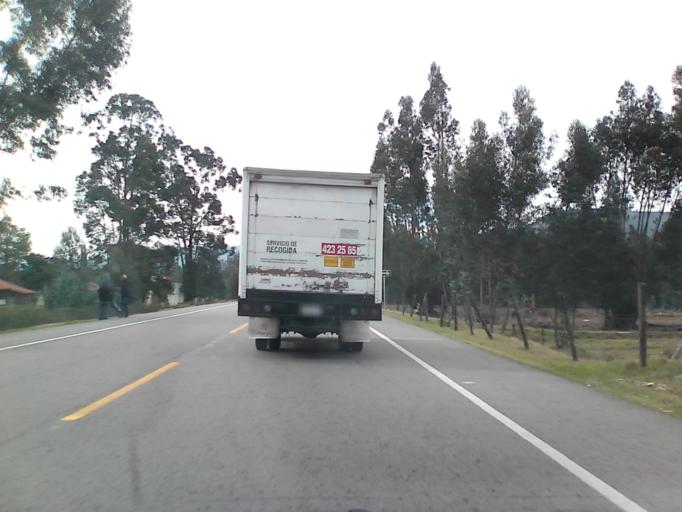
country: CO
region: Boyaca
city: Tibasosa
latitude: 5.7848
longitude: -72.9968
